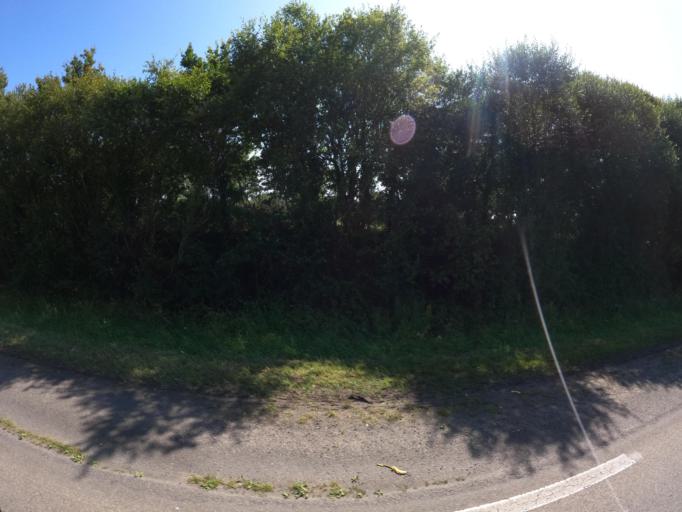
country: FR
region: Pays de la Loire
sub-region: Departement de la Loire-Atlantique
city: La Bernerie-en-Retz
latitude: 47.1061
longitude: -2.0557
